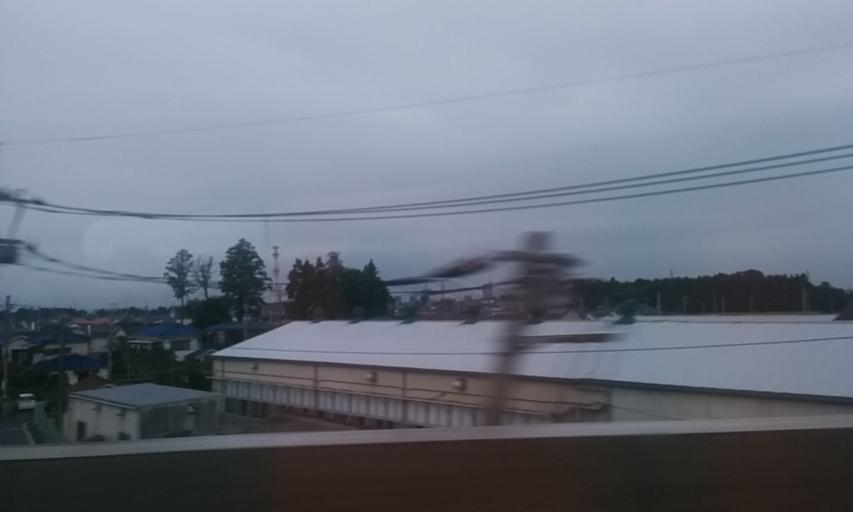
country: JP
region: Ibaraki
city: Koga
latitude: 36.1826
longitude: 139.7405
